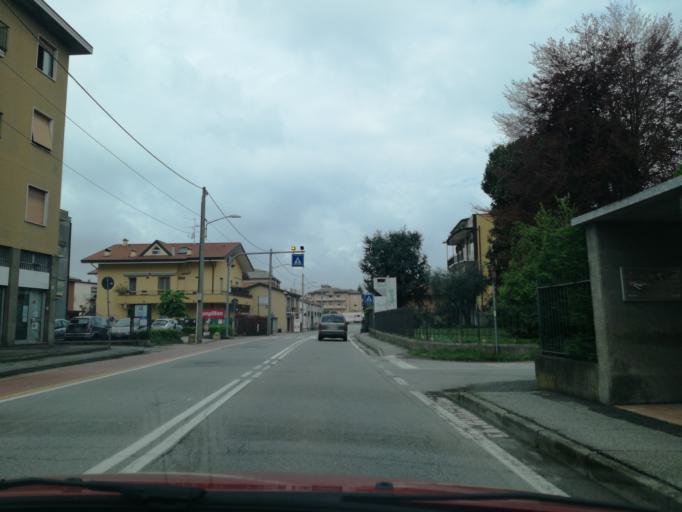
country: IT
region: Lombardy
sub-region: Provincia di Lecco
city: Cernusco Lombardone
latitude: 45.6973
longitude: 9.4088
